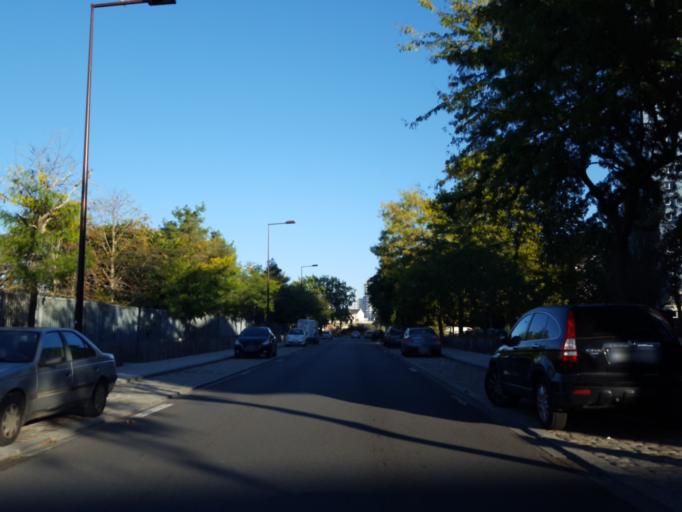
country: FR
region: Pays de la Loire
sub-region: Departement de la Loire-Atlantique
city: Nantes
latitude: 47.2094
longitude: -1.5313
